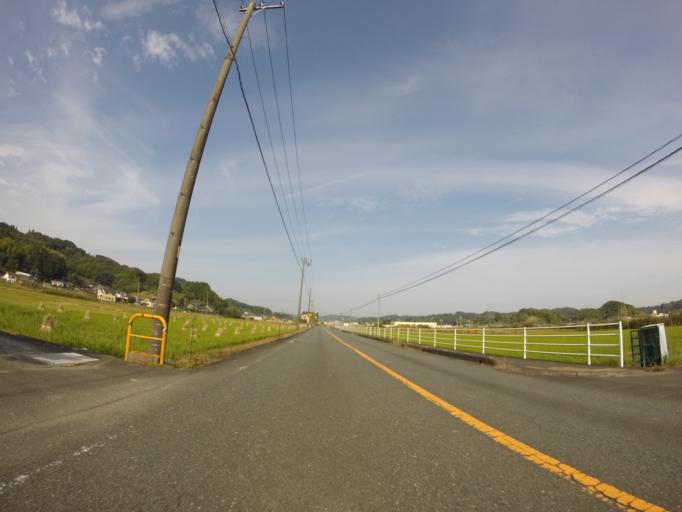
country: JP
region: Shizuoka
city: Shimada
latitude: 34.7626
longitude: 138.1893
